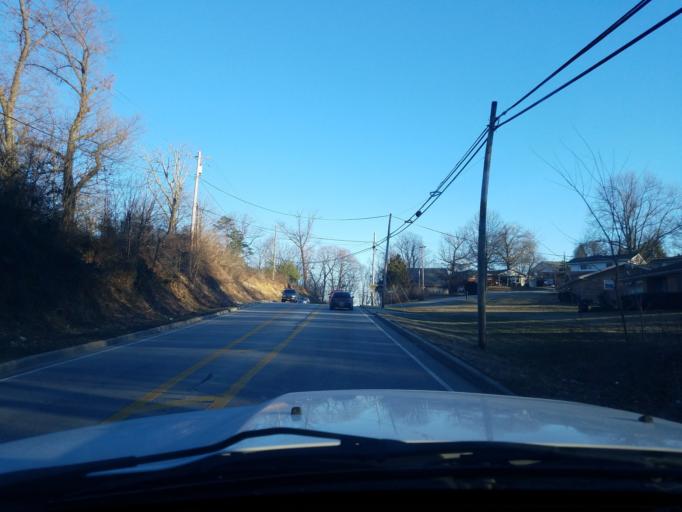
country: US
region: Indiana
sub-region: Floyd County
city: New Albany
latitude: 38.3246
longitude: -85.8592
